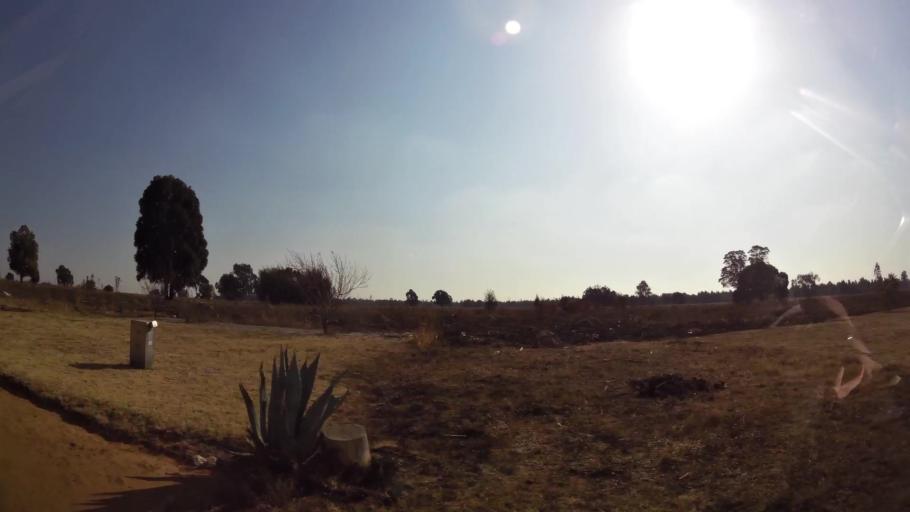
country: ZA
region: Gauteng
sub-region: West Rand District Municipality
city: Randfontein
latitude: -26.1837
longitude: 27.6771
